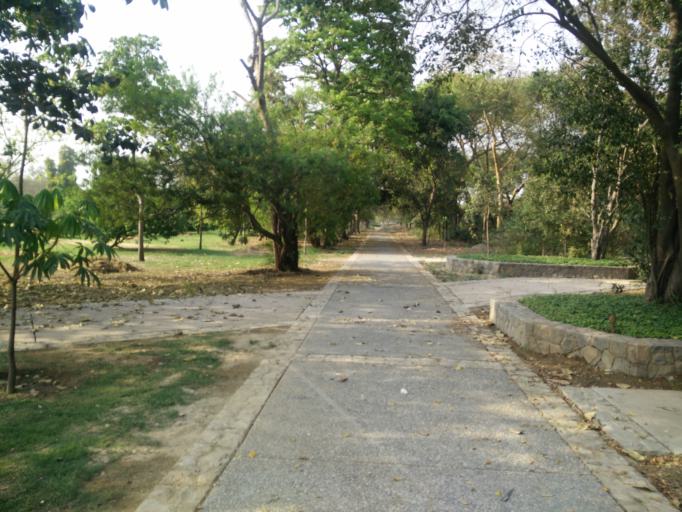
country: IN
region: NCT
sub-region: New Delhi
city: New Delhi
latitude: 28.5966
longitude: 77.2469
